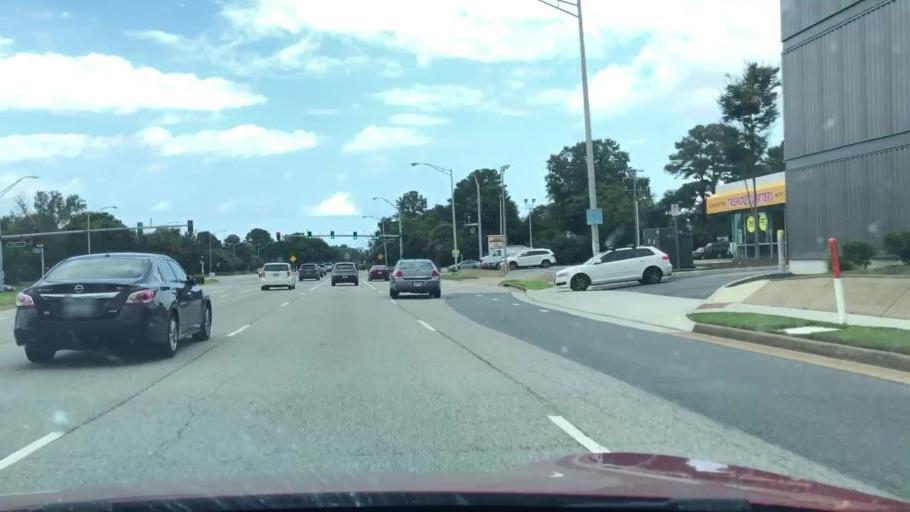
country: US
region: Virginia
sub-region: City of Chesapeake
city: Chesapeake
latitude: 36.8468
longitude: -76.1366
